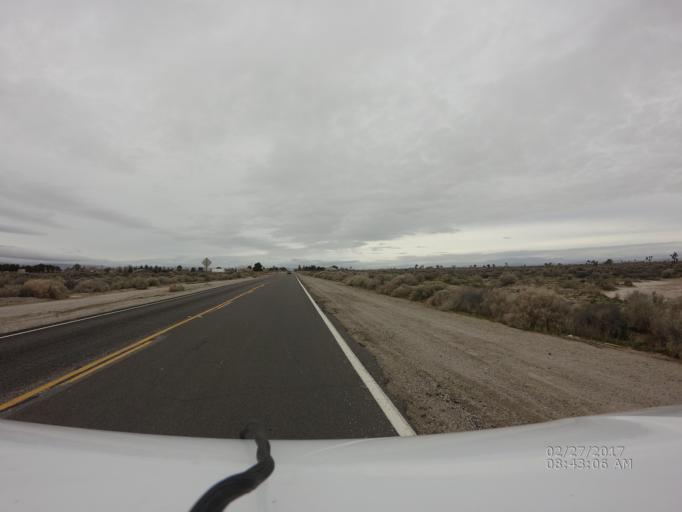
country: US
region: California
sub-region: Los Angeles County
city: Lancaster
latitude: 34.7192
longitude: -118.0605
